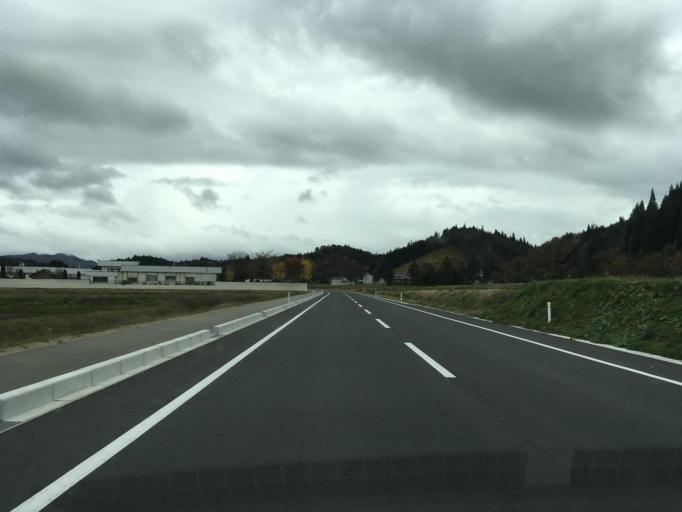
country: JP
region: Iwate
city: Ichinoseki
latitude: 39.0165
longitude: 141.3429
